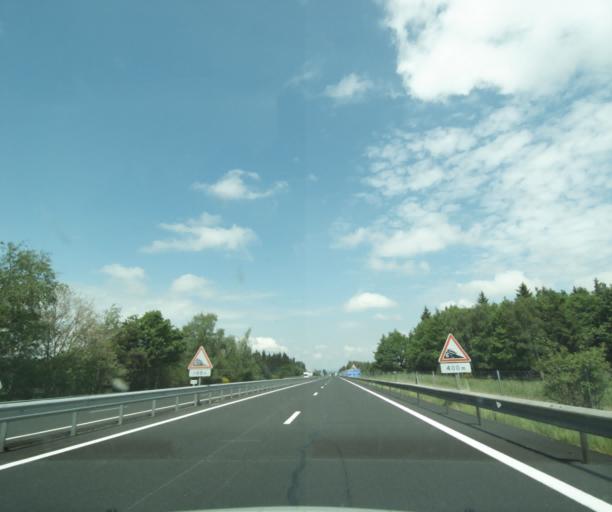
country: FR
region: Auvergne
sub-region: Departement du Cantal
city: Massiac
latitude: 45.1511
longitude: 3.1444
